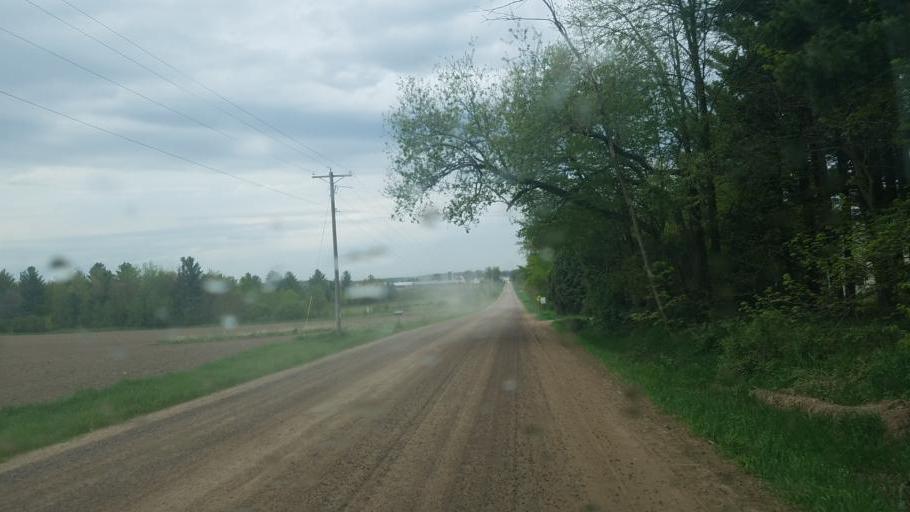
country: US
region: Wisconsin
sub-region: Clark County
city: Loyal
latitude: 44.6422
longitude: -90.4566
